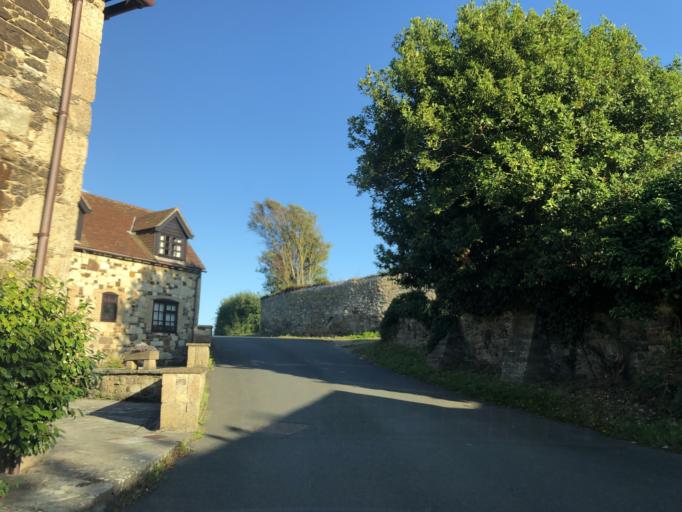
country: GB
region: England
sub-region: Isle of Wight
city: Shalfleet
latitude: 50.6389
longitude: -1.4001
